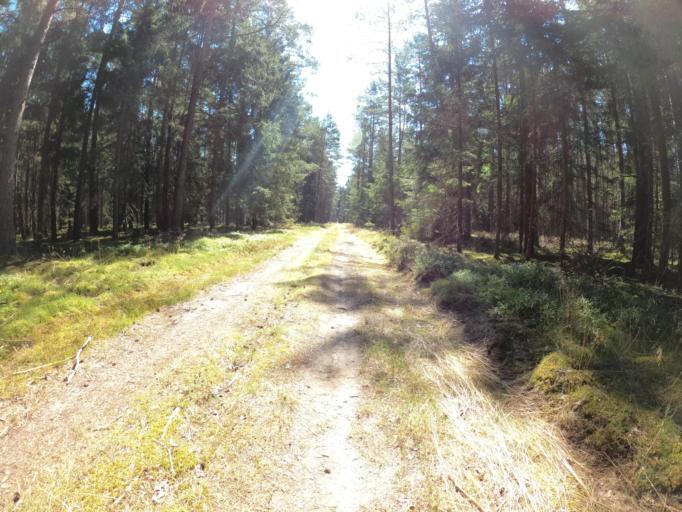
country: PL
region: West Pomeranian Voivodeship
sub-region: Powiat bialogardzki
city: Tychowo
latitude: 54.0620
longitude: 16.3665
